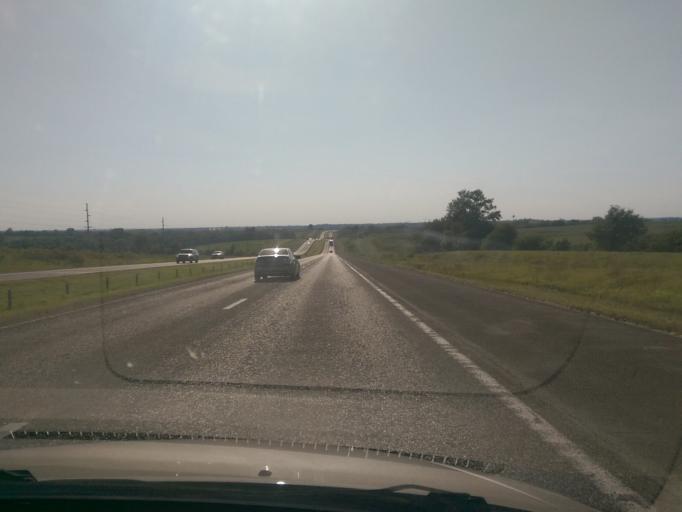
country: US
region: Missouri
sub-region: Lafayette County
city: Higginsville
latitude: 38.9926
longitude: -93.6863
